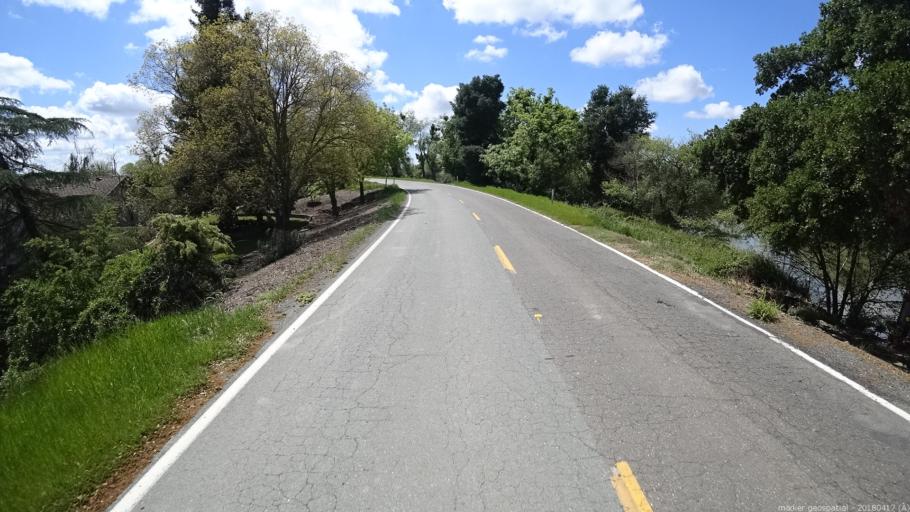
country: US
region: California
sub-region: Sacramento County
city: Walnut Grove
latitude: 38.2280
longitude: -121.5253
